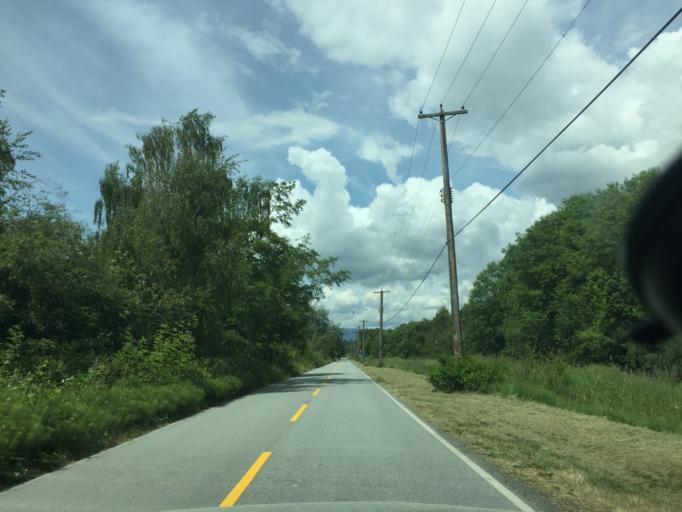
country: CA
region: British Columbia
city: Richmond
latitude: 49.2073
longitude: -123.1698
